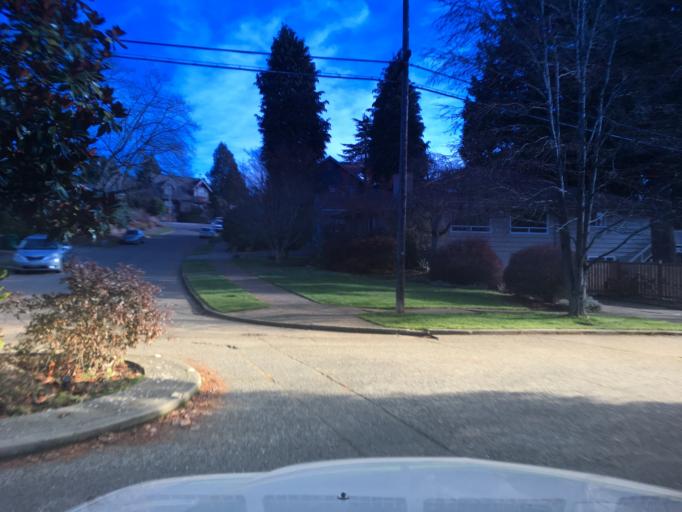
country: US
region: Washington
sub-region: King County
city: Inglewood-Finn Hill
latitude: 47.6740
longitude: -122.2796
